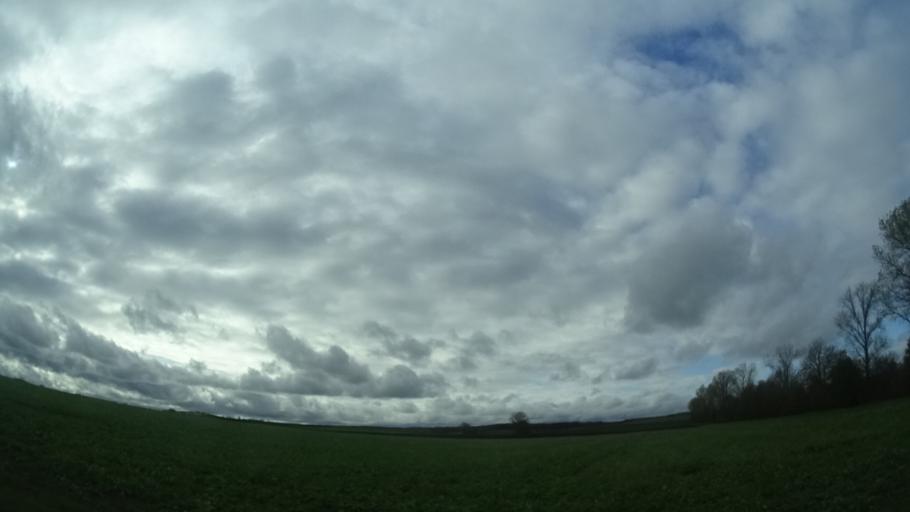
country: DE
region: Bavaria
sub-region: Regierungsbezirk Unterfranken
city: Hochheim
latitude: 50.3735
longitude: 10.4689
